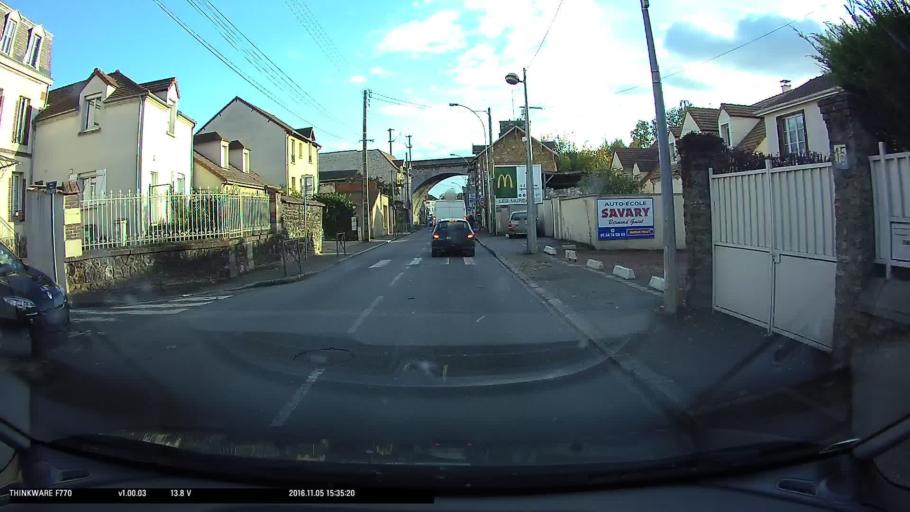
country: FR
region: Ile-de-France
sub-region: Departement des Yvelines
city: Meulan-en-Yvelines
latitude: 49.0072
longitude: 1.9054
